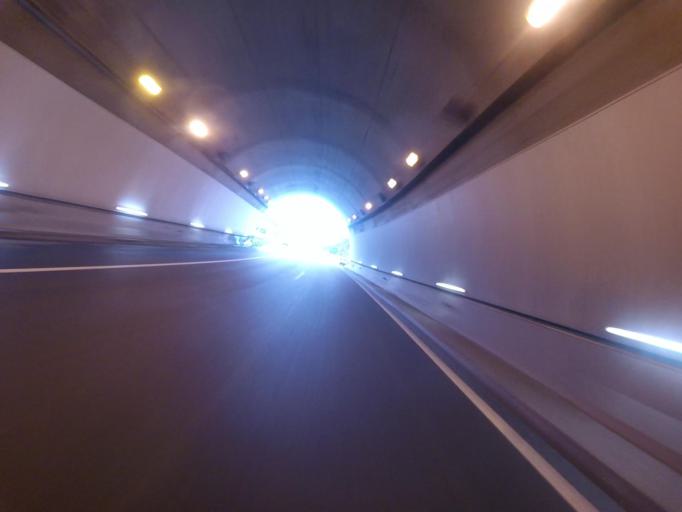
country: ES
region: Basque Country
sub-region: Provincia de Guipuzcoa
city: Errenteria
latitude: 43.3160
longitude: -1.9152
